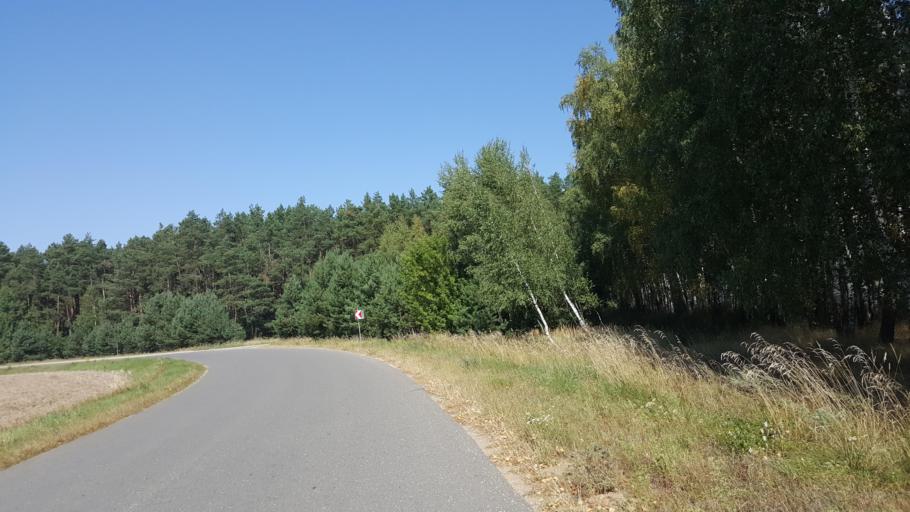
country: BY
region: Brest
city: Vysokaye
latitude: 52.4271
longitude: 23.4550
